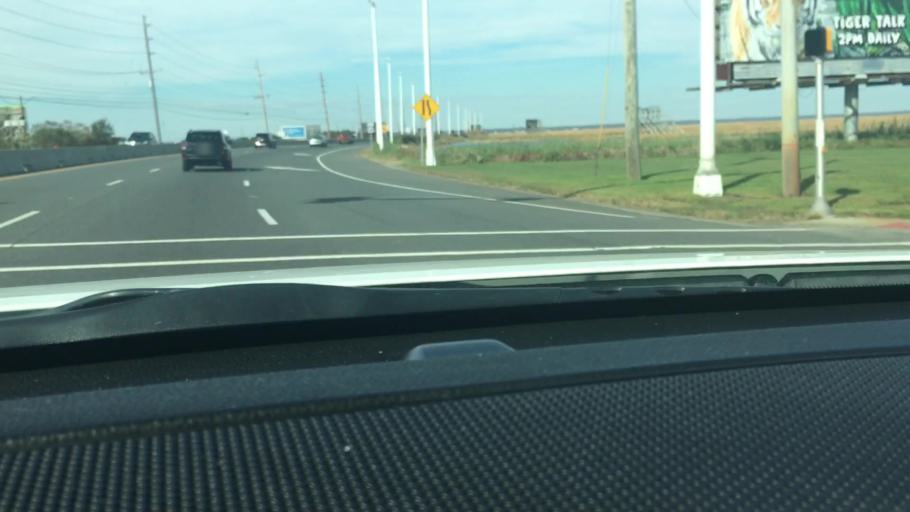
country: US
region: New Jersey
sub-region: Atlantic County
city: Atlantic City
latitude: 39.3794
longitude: -74.4574
